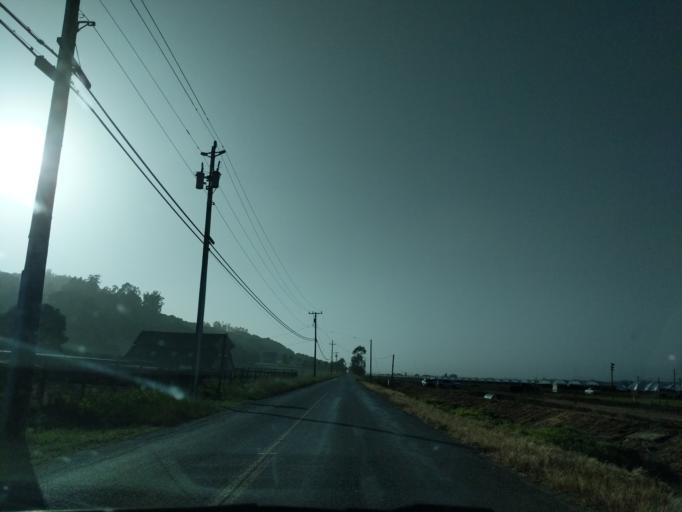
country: US
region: California
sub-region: San Benito County
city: Aromas
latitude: 36.8845
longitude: -121.6824
